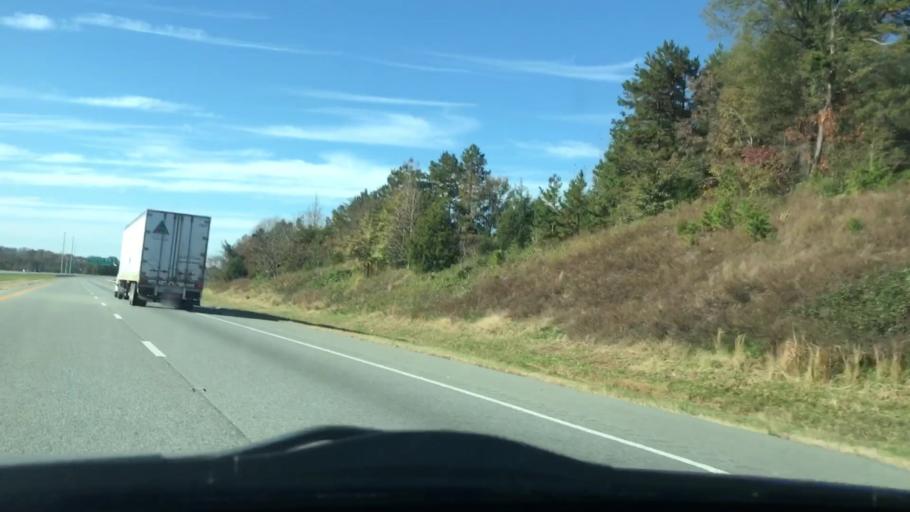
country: US
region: North Carolina
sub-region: Randolph County
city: Archdale
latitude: 35.9405
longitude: -79.9644
